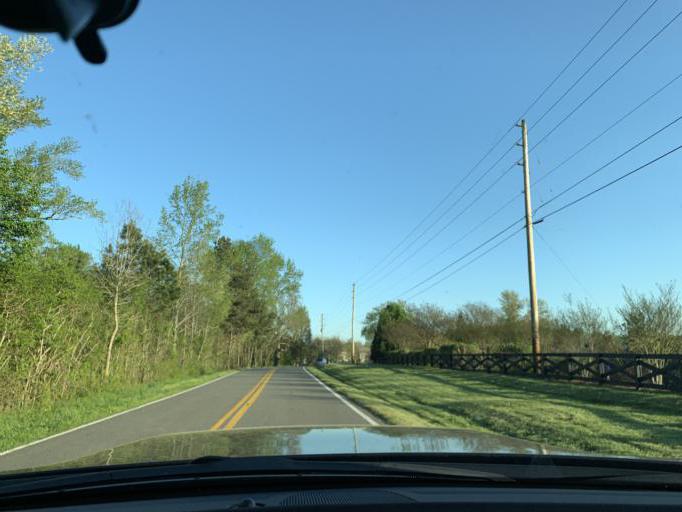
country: US
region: Georgia
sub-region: Forsyth County
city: Cumming
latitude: 34.2336
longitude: -84.2149
